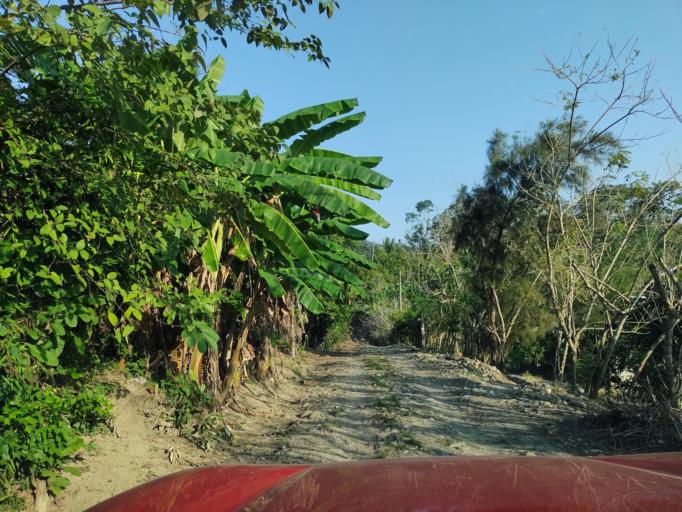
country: MX
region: Veracruz
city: Agua Dulce
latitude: 20.2830
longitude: -97.2490
